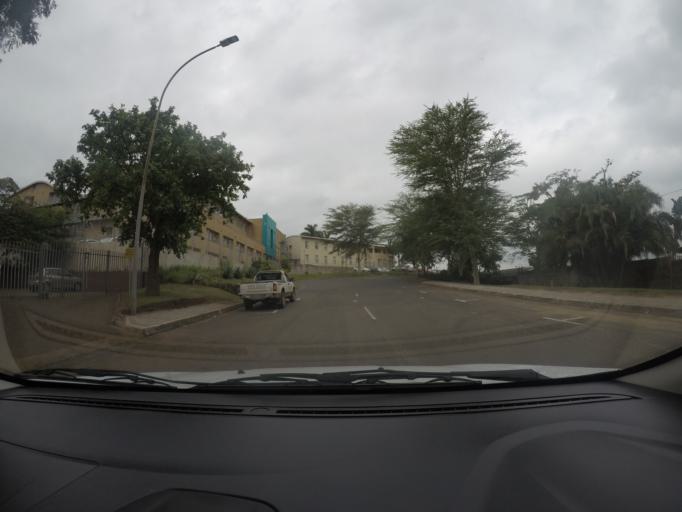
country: ZA
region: KwaZulu-Natal
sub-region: uThungulu District Municipality
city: Empangeni
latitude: -28.7411
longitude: 31.8957
